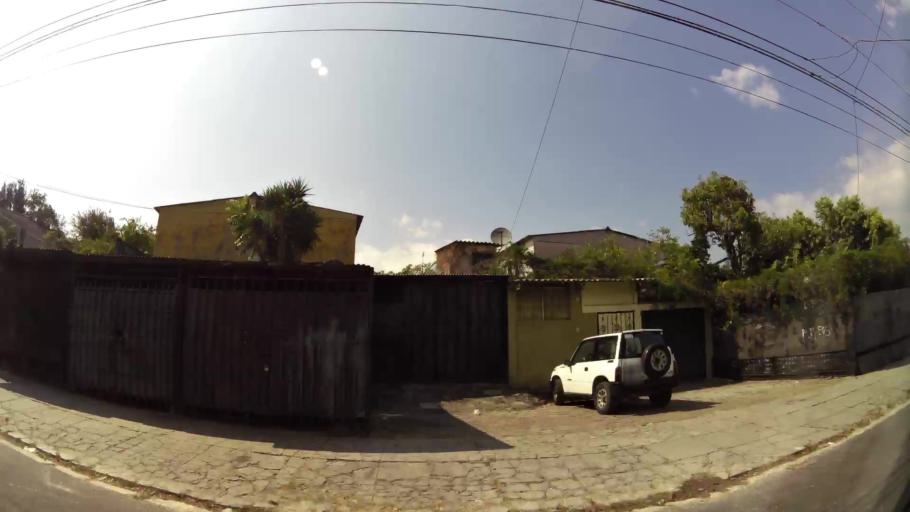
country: SV
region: San Salvador
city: Mejicanos
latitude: 13.7210
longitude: -89.2131
